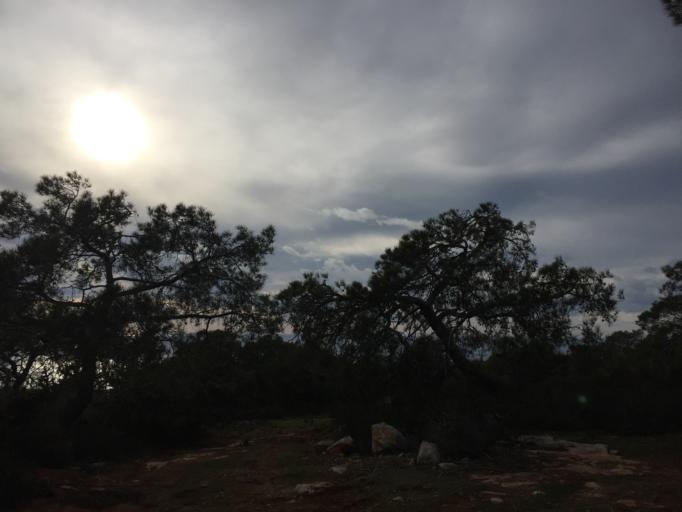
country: CY
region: Pafos
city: Pegeia
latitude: 34.8900
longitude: 32.3740
